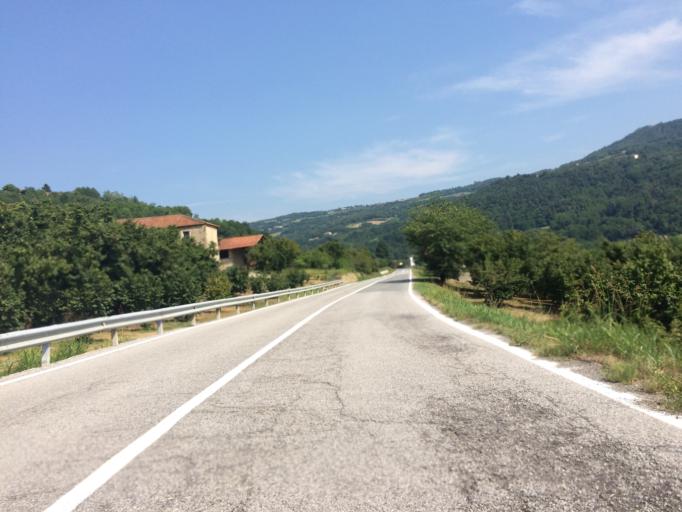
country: IT
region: Piedmont
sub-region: Provincia di Cuneo
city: Torre Bormida
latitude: 44.5611
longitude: 8.1494
